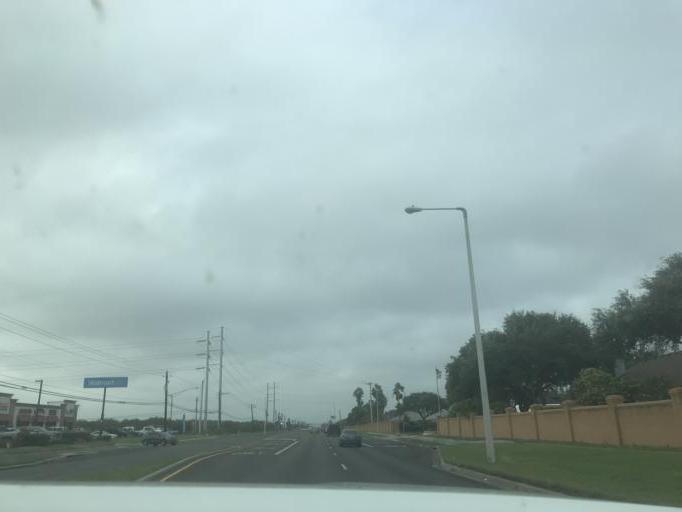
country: US
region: Texas
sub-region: Nueces County
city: Corpus Christi
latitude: 27.6805
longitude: -97.3737
